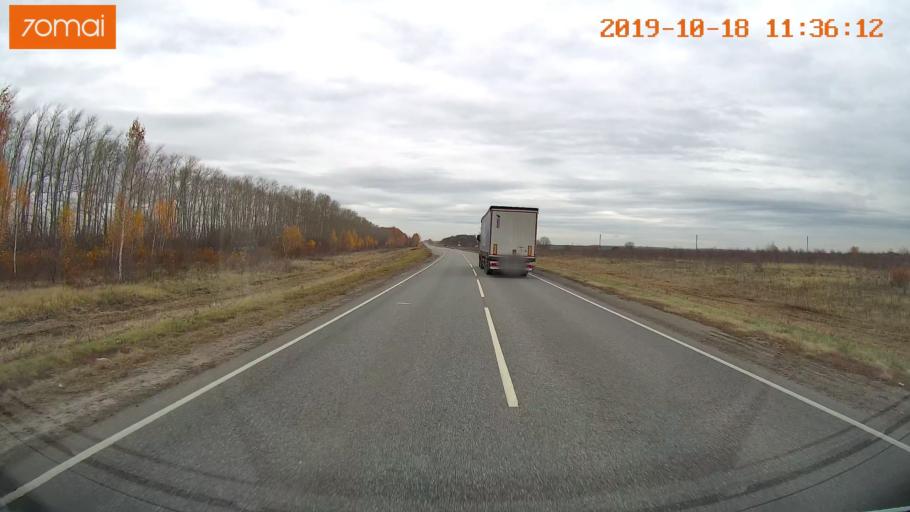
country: RU
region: Rjazan
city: Oktyabr'skiy
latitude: 54.1385
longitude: 38.8014
